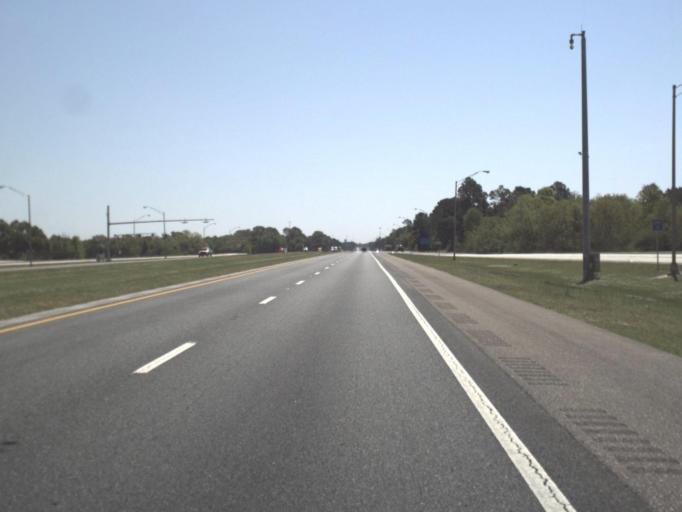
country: US
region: Florida
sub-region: Escambia County
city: Cantonment
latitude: 30.5533
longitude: -87.3623
